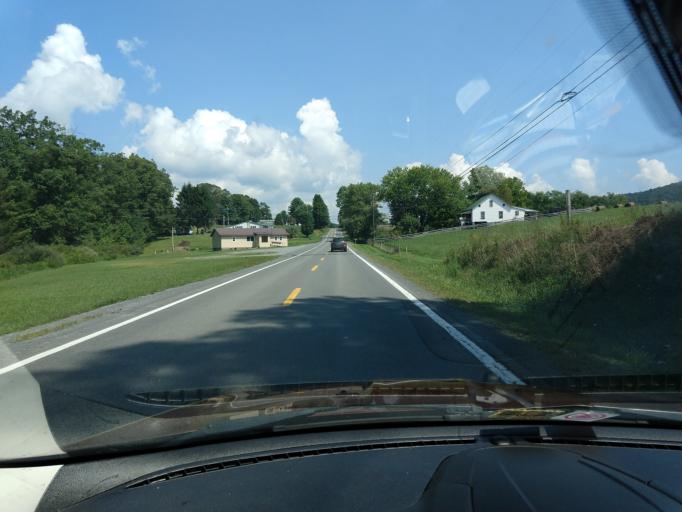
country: US
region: West Virginia
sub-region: Greenbrier County
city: Fairlea
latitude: 37.8447
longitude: -80.5518
